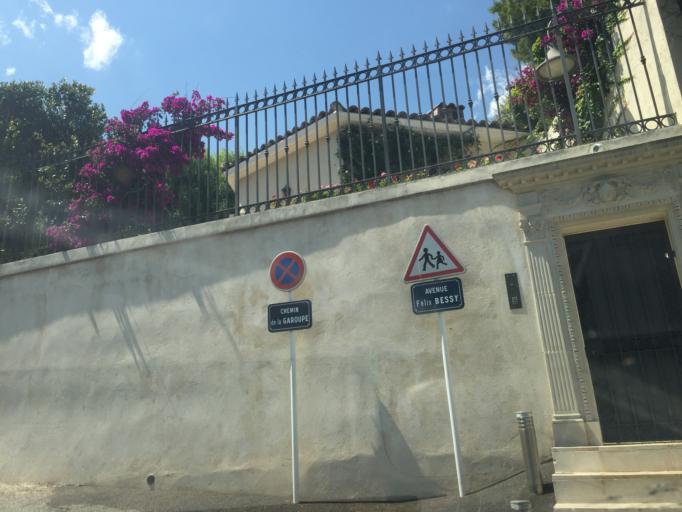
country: FR
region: Provence-Alpes-Cote d'Azur
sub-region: Departement des Alpes-Maritimes
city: Antibes
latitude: 43.5562
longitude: 7.1318
